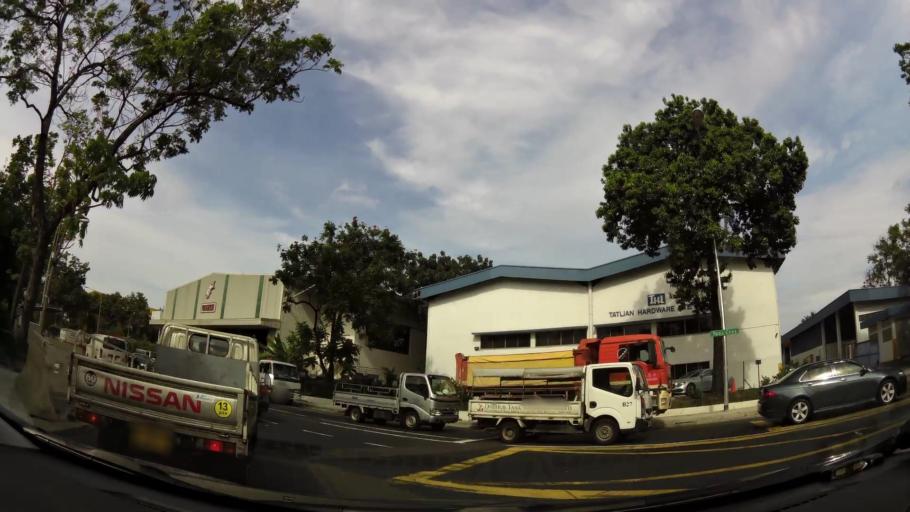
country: MY
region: Johor
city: Johor Bahru
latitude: 1.3194
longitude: 103.6490
